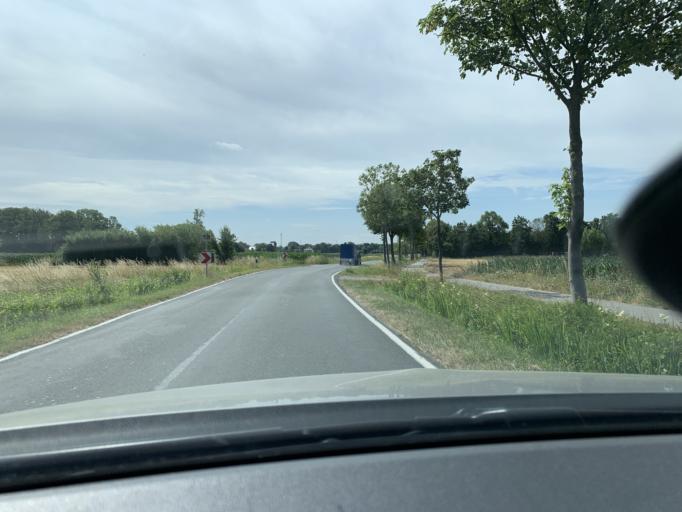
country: DE
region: North Rhine-Westphalia
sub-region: Regierungsbezirk Arnsberg
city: Lippstadt
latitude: 51.6817
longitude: 8.3954
